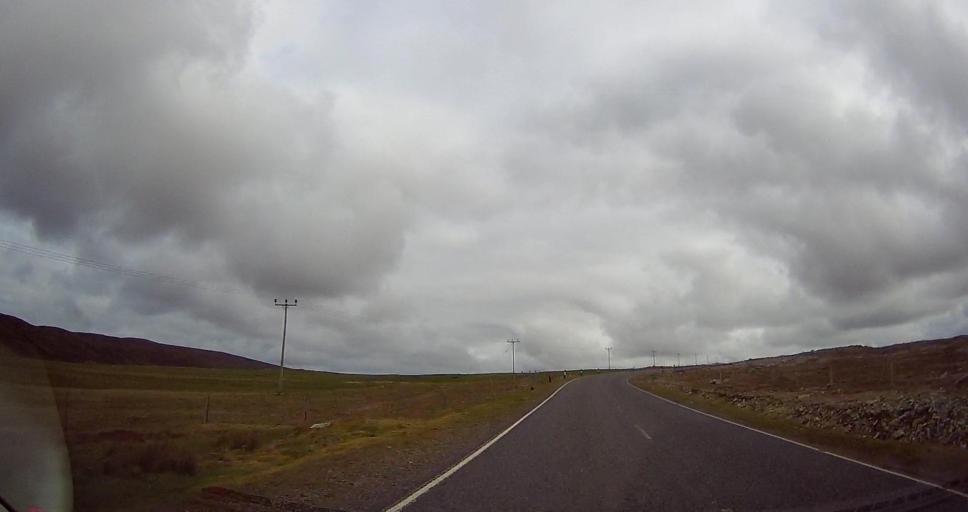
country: GB
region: Scotland
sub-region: Shetland Islands
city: Shetland
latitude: 60.7219
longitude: -0.9096
